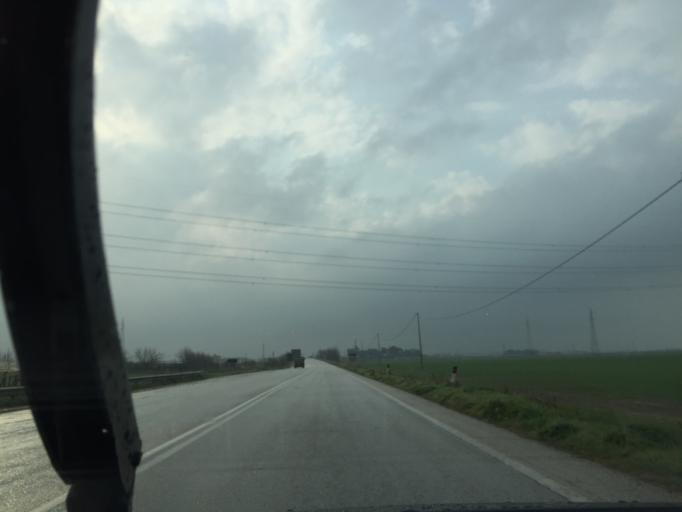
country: IT
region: Apulia
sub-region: Provincia di Foggia
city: Foggia
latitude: 41.4966
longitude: 15.5199
